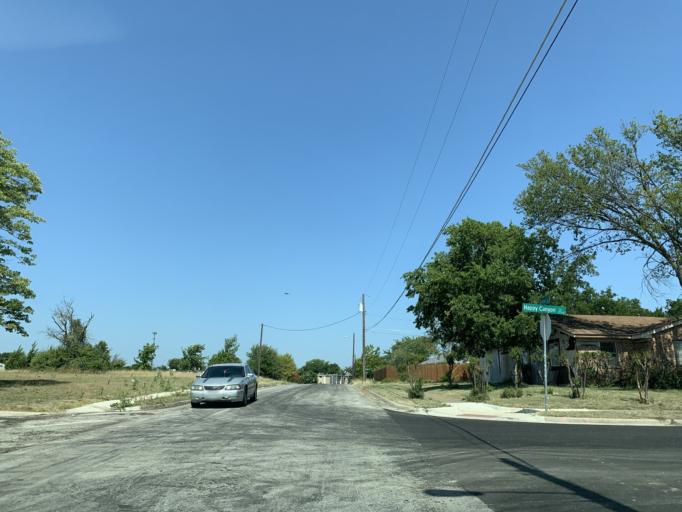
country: US
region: Texas
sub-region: Dallas County
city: Hutchins
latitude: 32.6709
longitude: -96.7583
